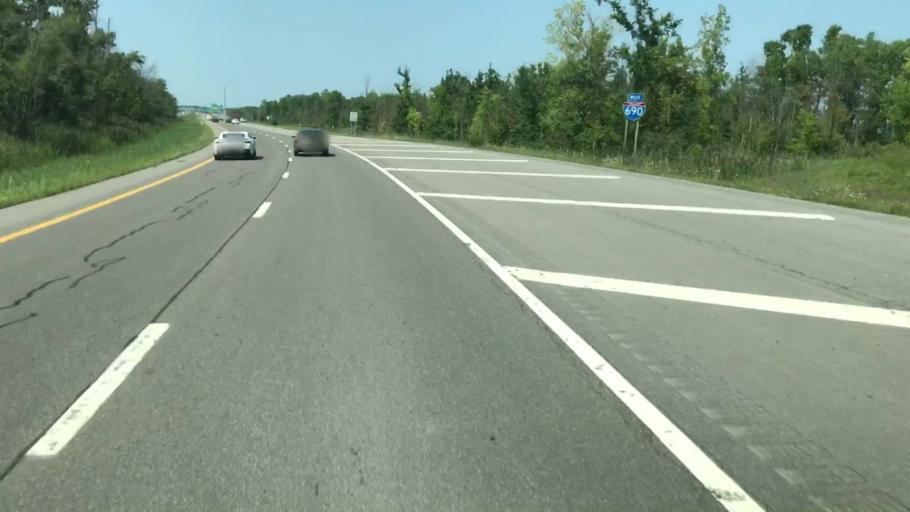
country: US
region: New York
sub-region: Onondaga County
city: East Syracuse
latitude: 43.0565
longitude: -76.0552
